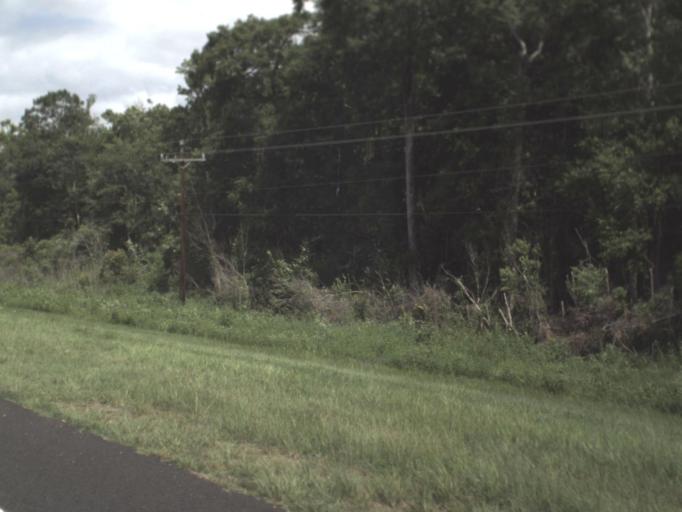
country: US
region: Florida
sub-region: Nassau County
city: Yulee
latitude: 30.6296
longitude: -81.5693
